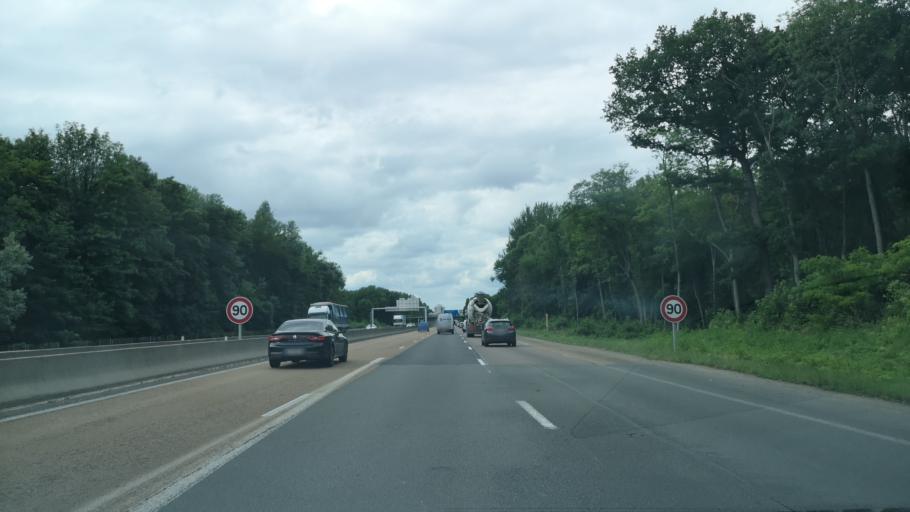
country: FR
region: Champagne-Ardenne
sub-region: Departement de la Marne
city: Cormontreuil
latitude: 49.2260
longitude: 4.0592
